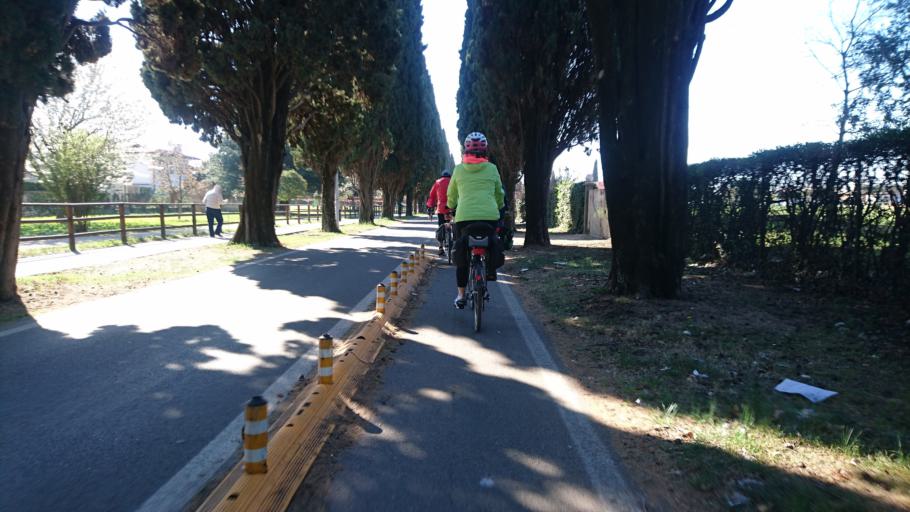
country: IT
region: Veneto
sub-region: Provincia di Vicenza
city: Bassano del Grappa
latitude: 45.7531
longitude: 11.7349
